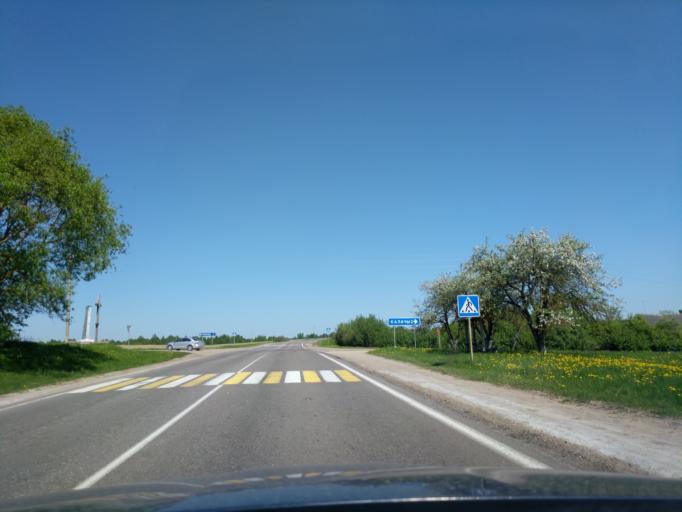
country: BY
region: Minsk
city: Il'ya
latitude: 54.2986
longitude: 27.4790
